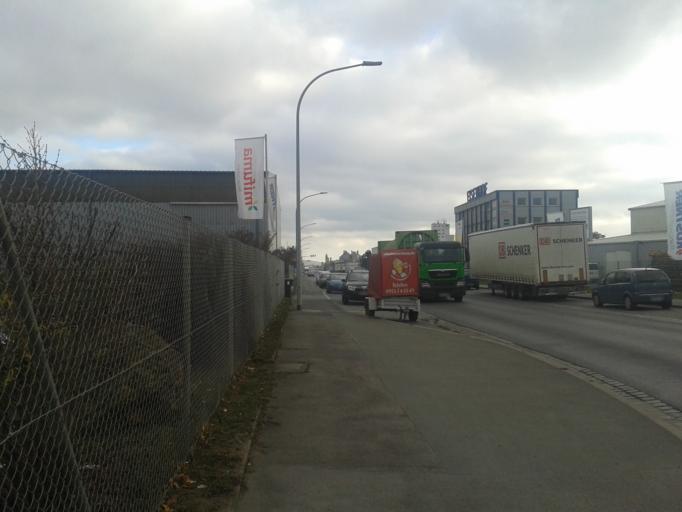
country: DE
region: Bavaria
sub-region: Upper Franconia
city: Hallstadt
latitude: 49.9128
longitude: 10.8639
